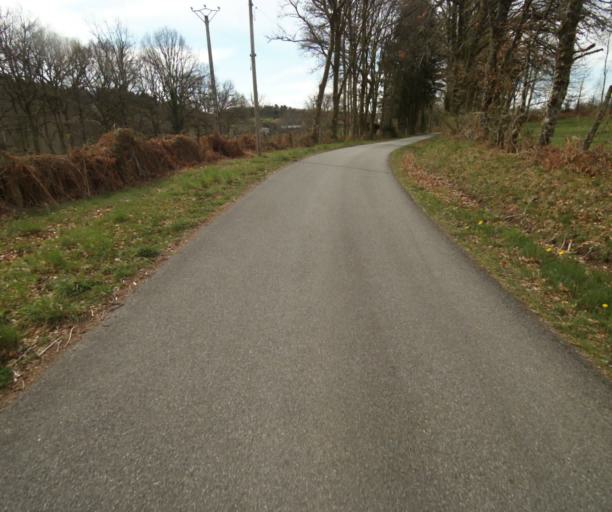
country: FR
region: Limousin
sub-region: Departement de la Correze
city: Correze
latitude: 45.3898
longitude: 1.8979
